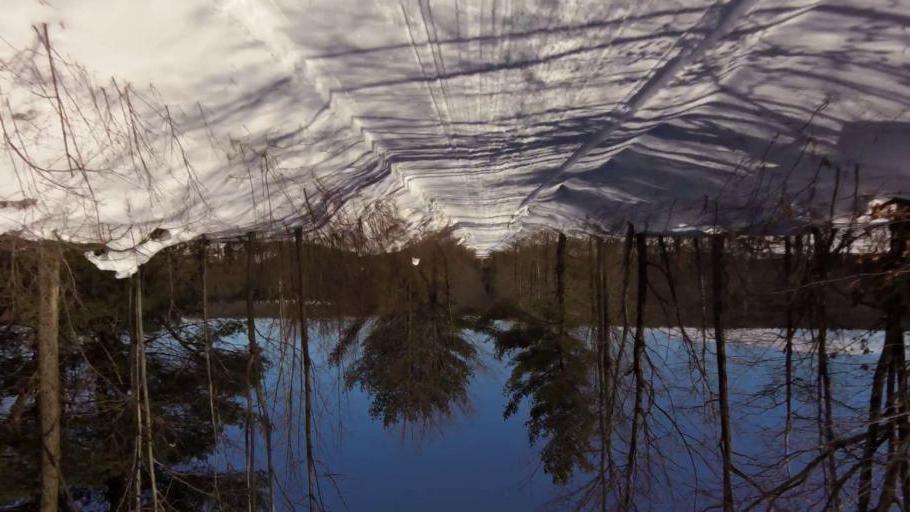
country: US
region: New York
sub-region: Allegany County
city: Cuba
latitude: 42.3267
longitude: -78.2466
